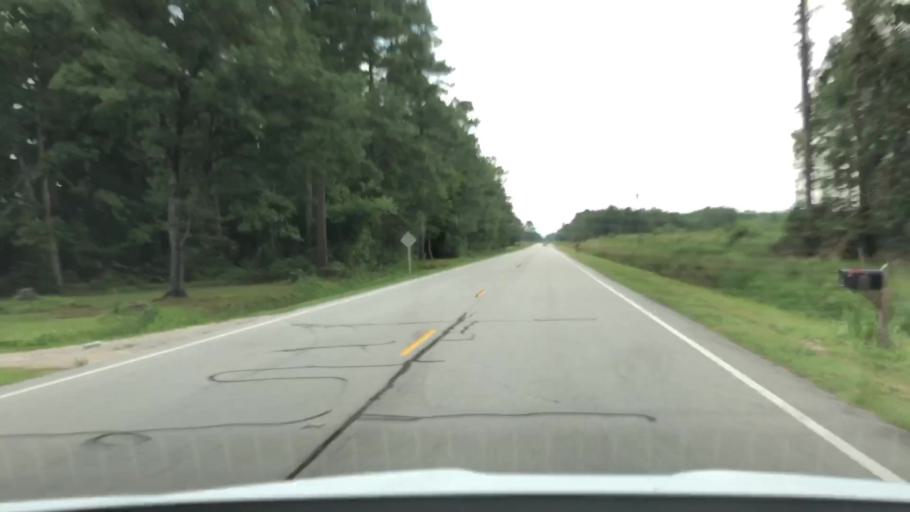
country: US
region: North Carolina
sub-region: Lenoir County
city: Kinston
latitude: 35.1220
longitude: -77.5179
